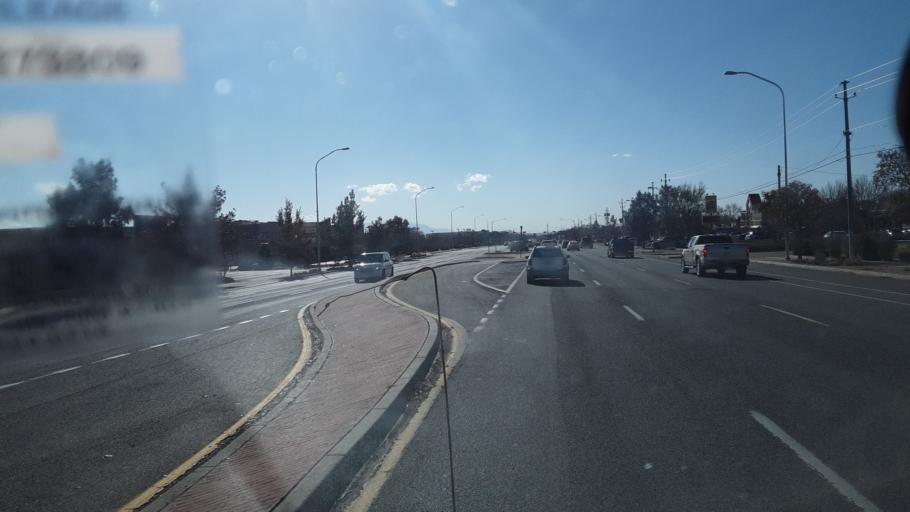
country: US
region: New Mexico
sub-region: Santa Fe County
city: Agua Fria
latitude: 35.6516
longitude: -105.9978
